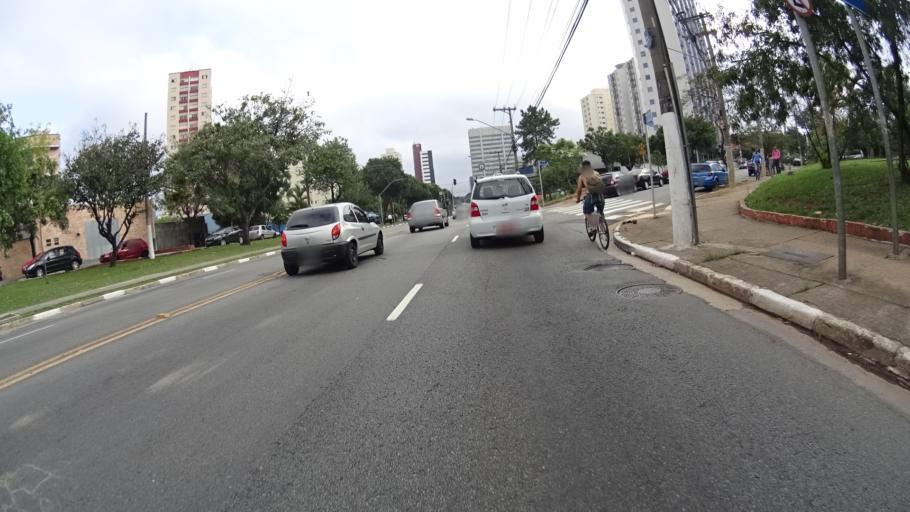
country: BR
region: Sao Paulo
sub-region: Diadema
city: Diadema
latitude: -23.6301
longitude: -46.6415
